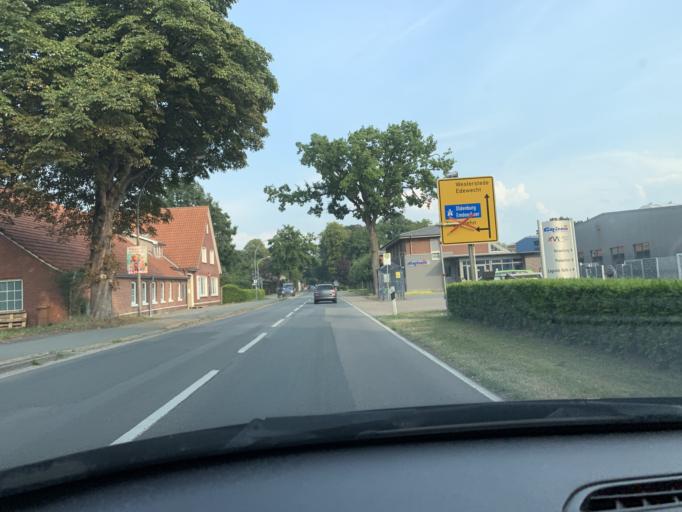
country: DE
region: Lower Saxony
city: Barssel
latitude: 53.1767
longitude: 7.7636
